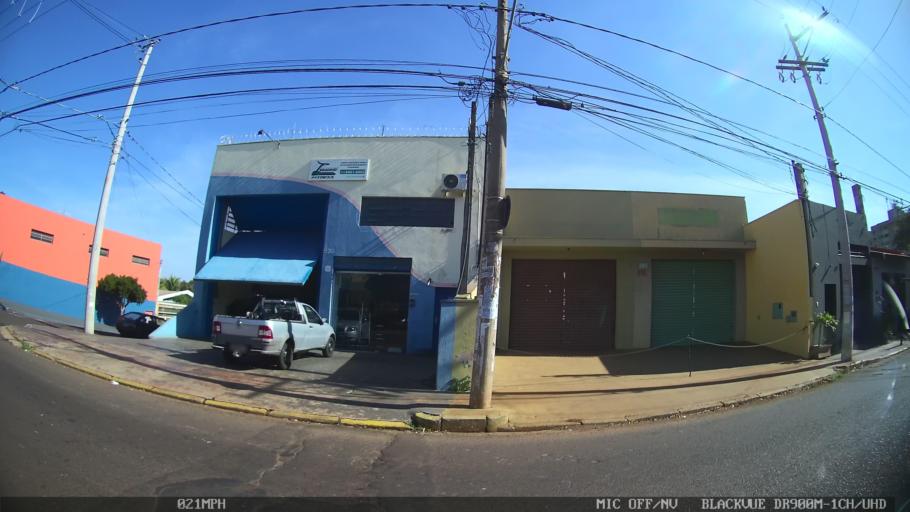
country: BR
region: Sao Paulo
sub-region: Ribeirao Preto
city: Ribeirao Preto
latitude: -21.1803
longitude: -47.7762
